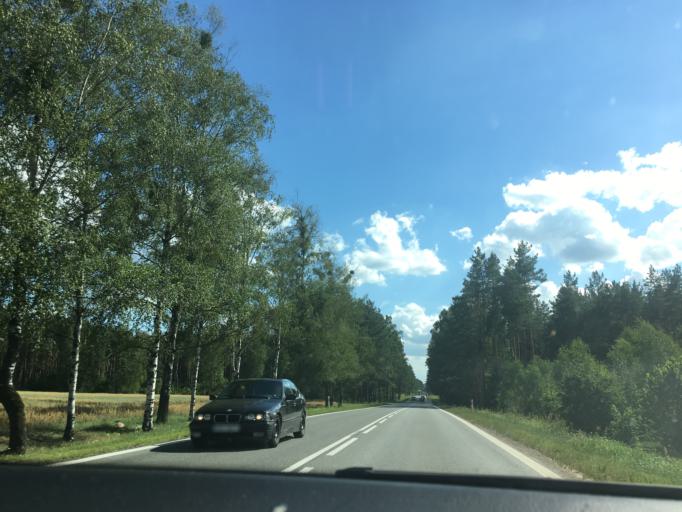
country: PL
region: Podlasie
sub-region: Powiat sokolski
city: Janow
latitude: 53.3664
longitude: 23.1073
